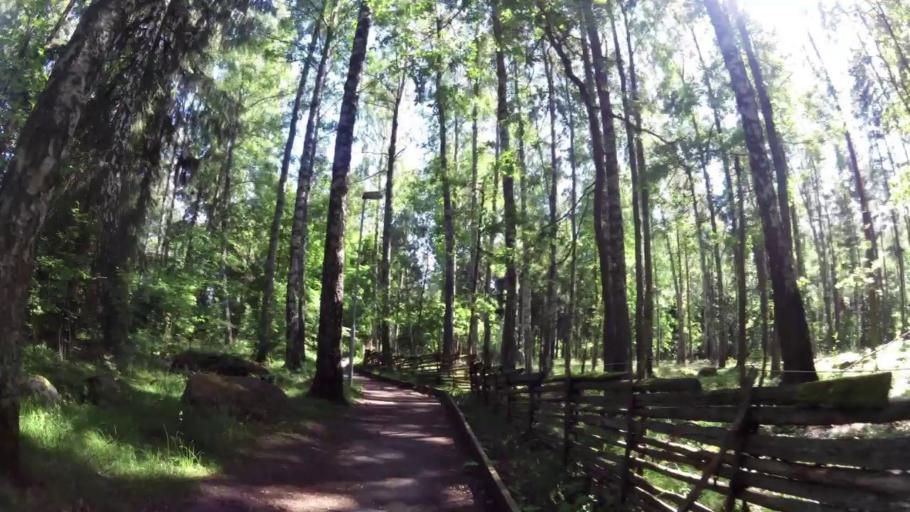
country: SE
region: OEstergoetland
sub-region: Linkopings Kommun
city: Linkoping
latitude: 58.4036
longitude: 15.5921
